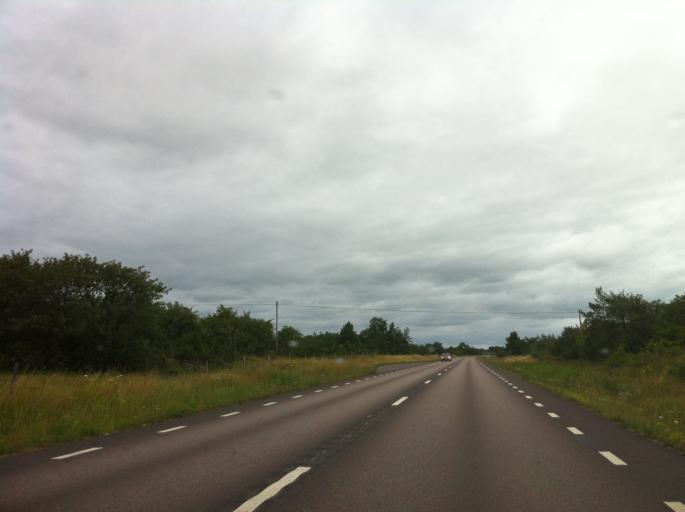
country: SE
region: Kalmar
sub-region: Borgholms Kommun
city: Borgholm
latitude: 57.0876
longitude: 16.9231
